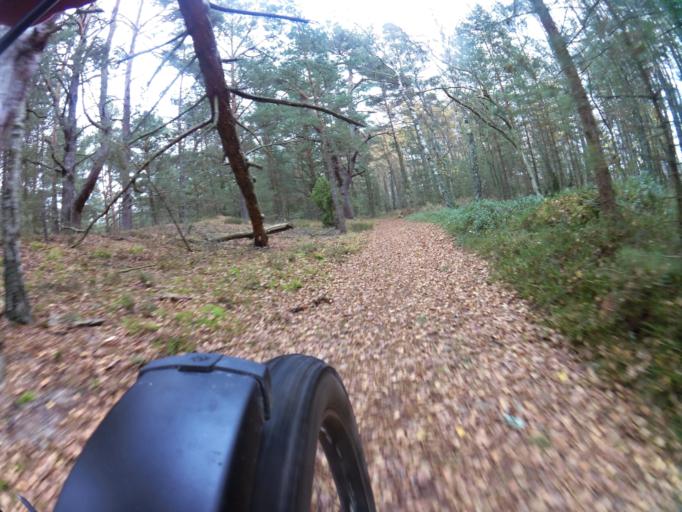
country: PL
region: Pomeranian Voivodeship
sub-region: Powiat leborski
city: Leba
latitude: 54.7674
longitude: 17.6121
